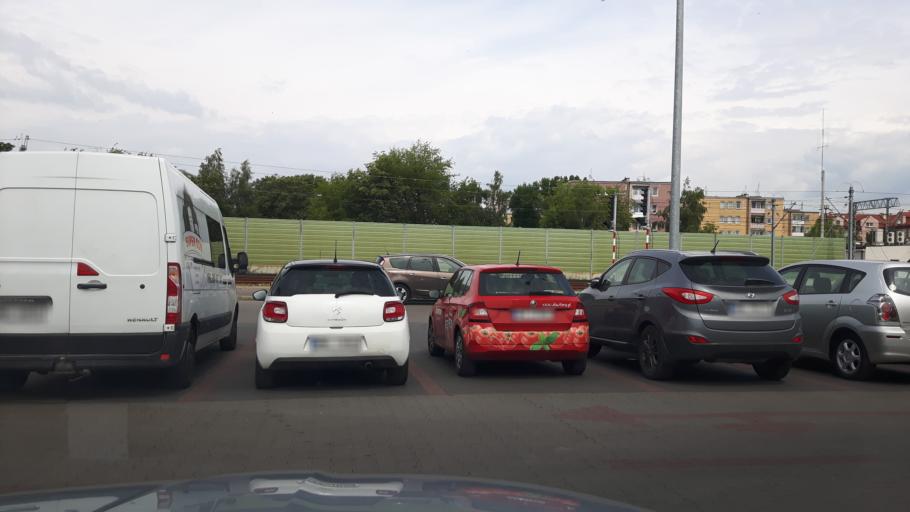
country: PL
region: Masovian Voivodeship
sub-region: Powiat wolominski
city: Wolomin
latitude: 52.3485
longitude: 21.2440
